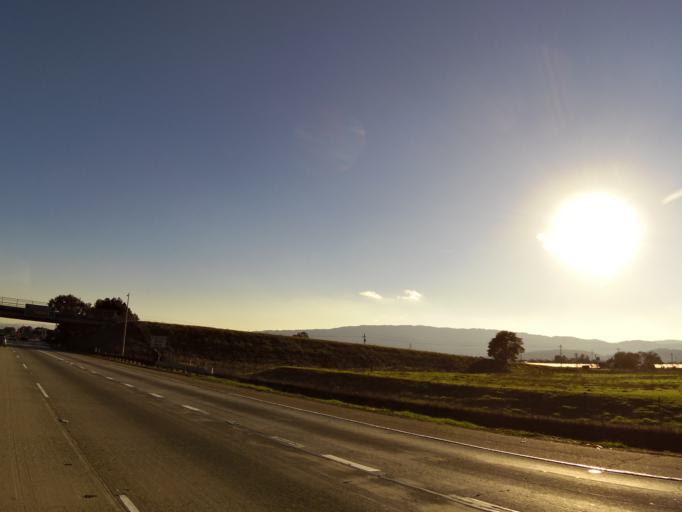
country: US
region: California
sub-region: Santa Clara County
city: Gilroy
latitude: 37.0447
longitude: -121.5784
